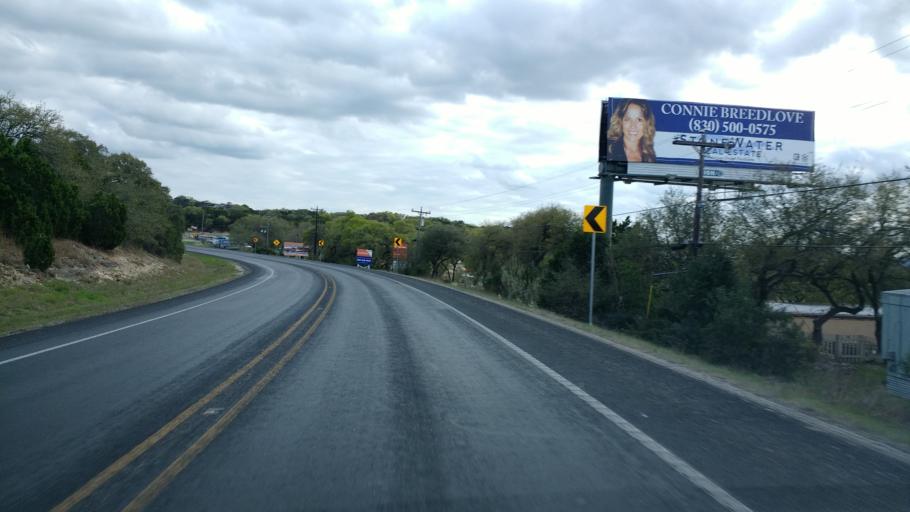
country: US
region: Texas
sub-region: Comal County
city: Canyon Lake
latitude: 29.8923
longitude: -98.2115
